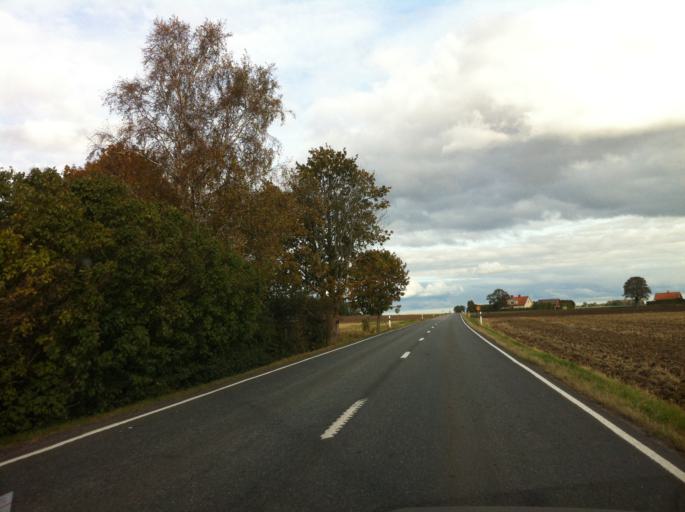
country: SE
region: OEstergoetland
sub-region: Vadstena Kommun
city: Herrestad
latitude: 58.3826
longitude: 14.7522
